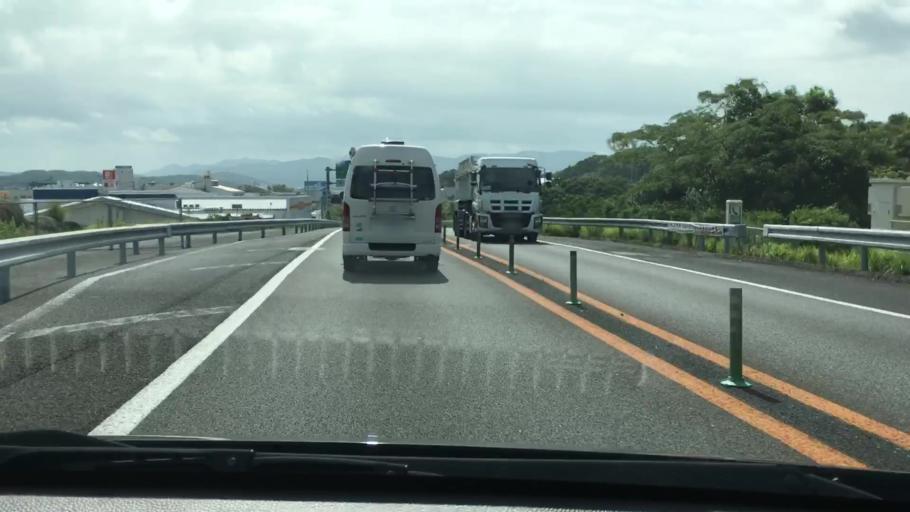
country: JP
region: Nagasaki
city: Sasebo
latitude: 33.1505
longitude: 129.7666
